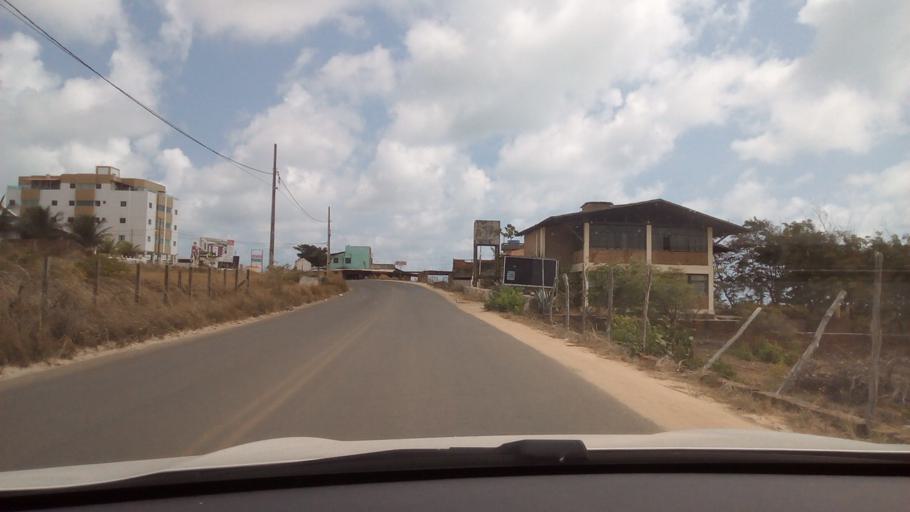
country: BR
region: Paraiba
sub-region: Conde
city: Conde
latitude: -7.2922
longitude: -34.8072
